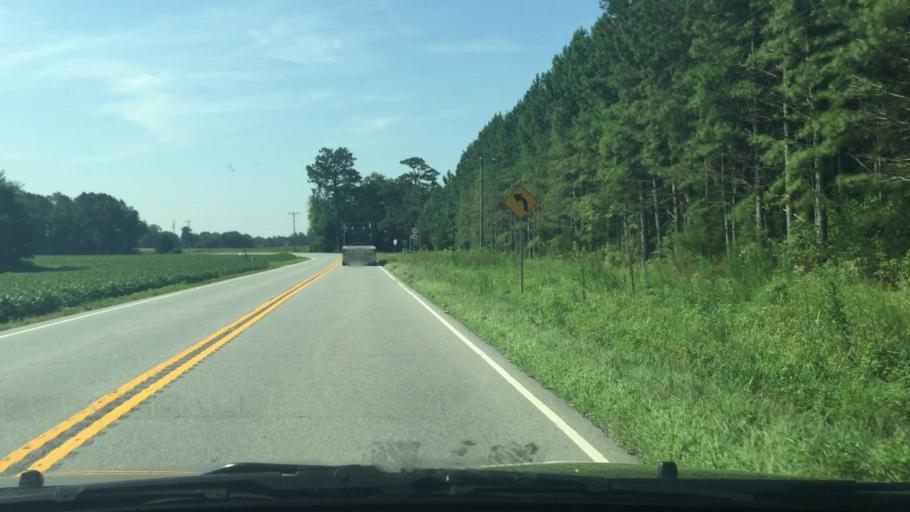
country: US
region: Virginia
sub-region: Sussex County
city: Sussex
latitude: 36.8871
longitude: -77.1543
